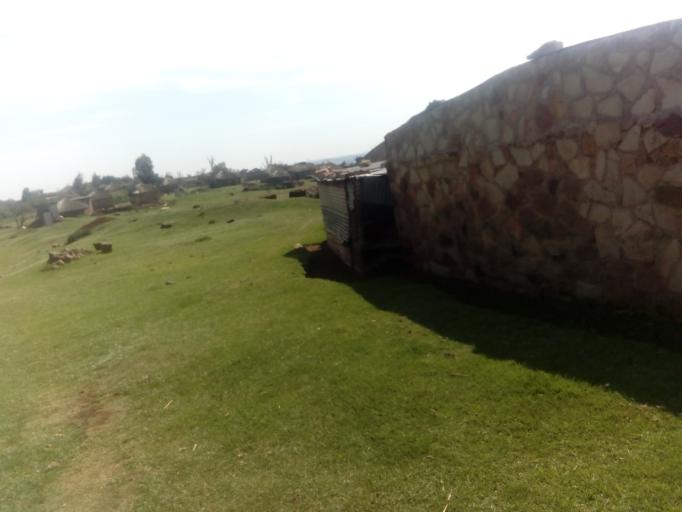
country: LS
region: Berea
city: Teyateyaneng
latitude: -29.2293
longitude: 27.8693
